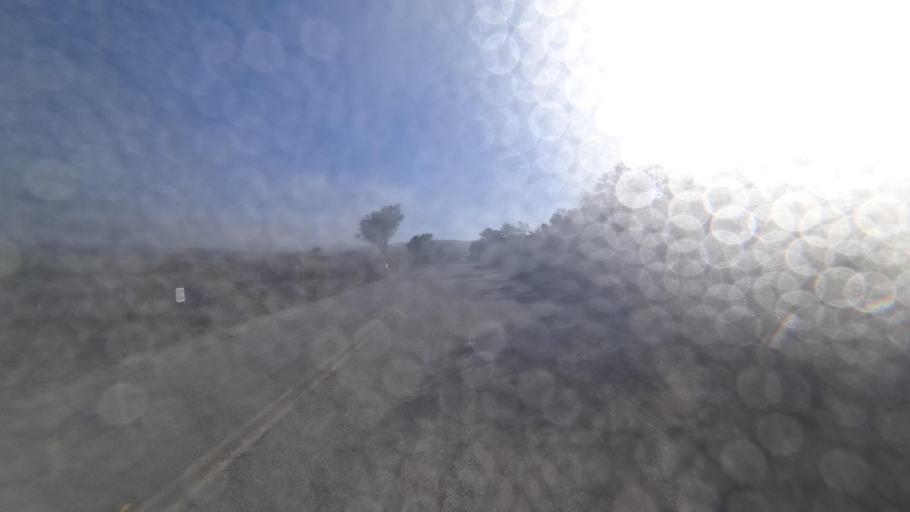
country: US
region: California
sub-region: Monterey County
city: Del Rey Oaks
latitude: 36.5812
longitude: -121.7817
